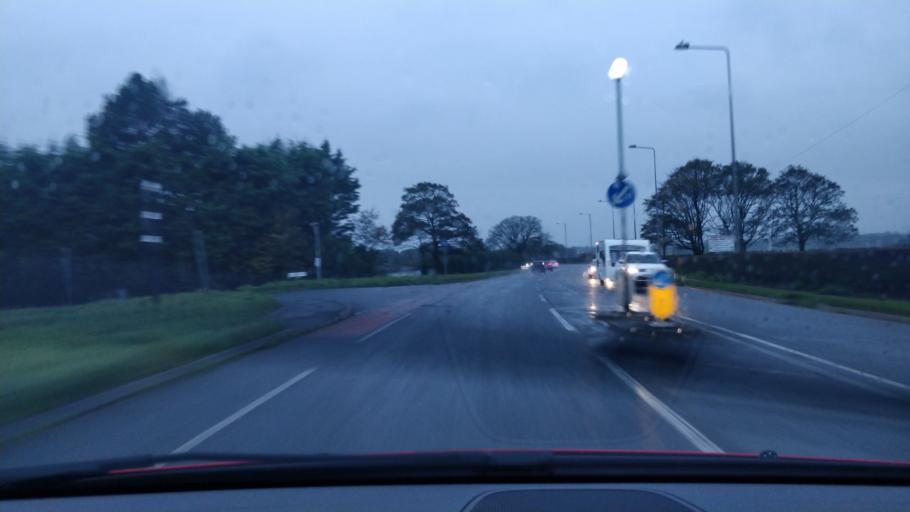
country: GB
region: England
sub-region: Lancashire
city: Fylde
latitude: 53.7864
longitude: -2.9429
